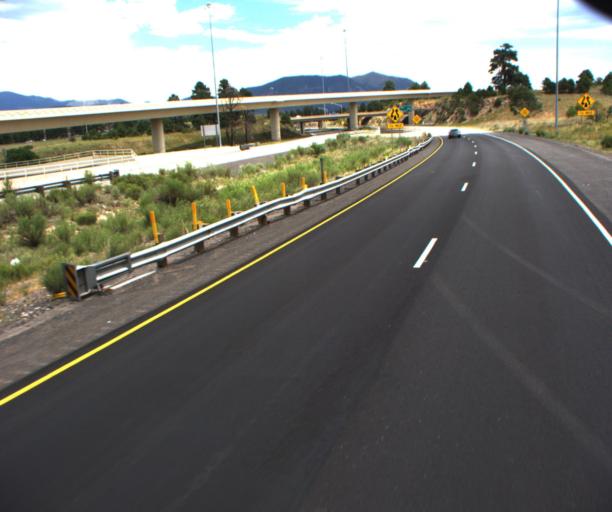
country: US
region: Arizona
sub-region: Coconino County
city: Flagstaff
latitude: 35.1695
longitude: -111.6641
